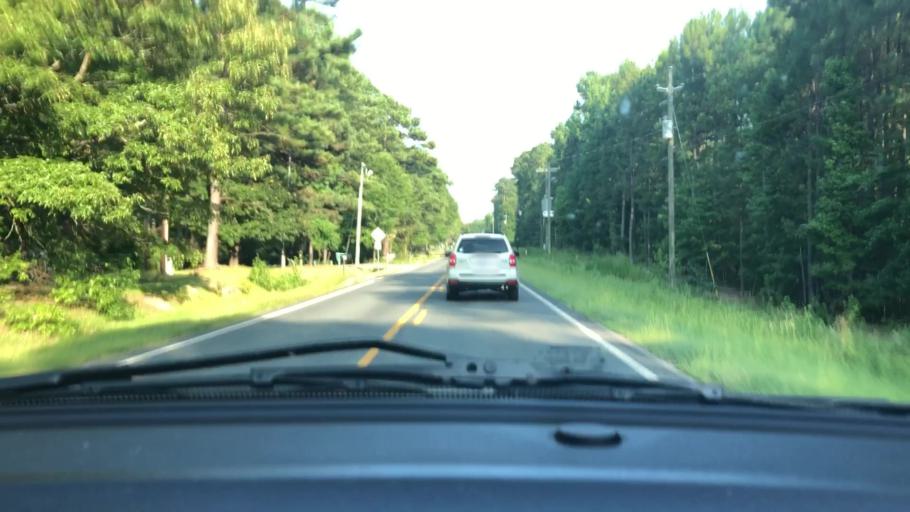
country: US
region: North Carolina
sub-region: Lee County
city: Broadway
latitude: 35.3594
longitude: -79.0839
